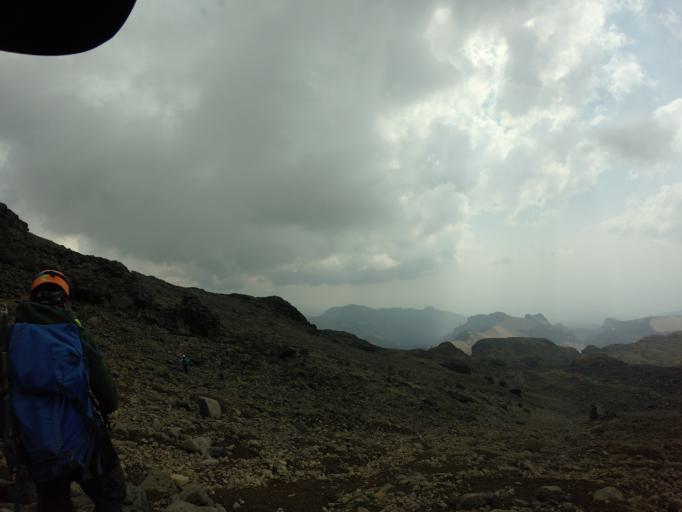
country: MX
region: Mexico
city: Amecameca de Juarez
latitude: 19.1549
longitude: -98.6416
